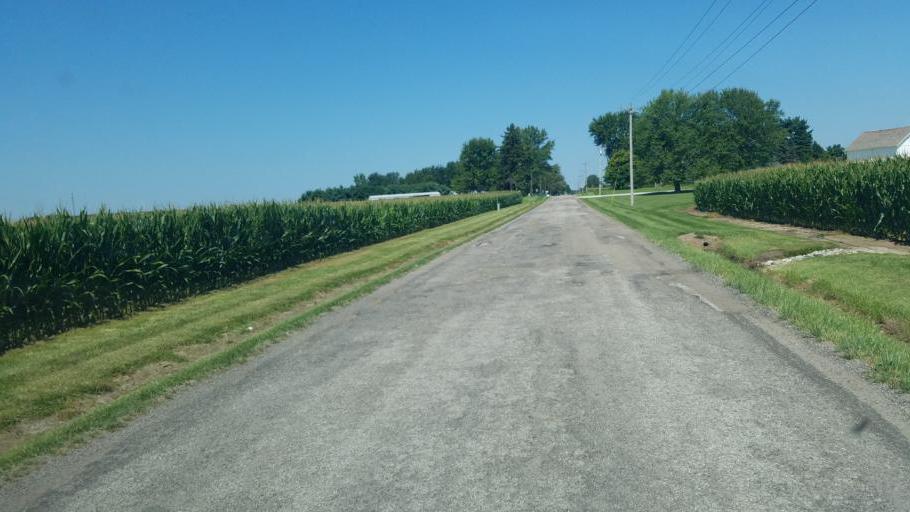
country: US
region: Ohio
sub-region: Delaware County
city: Ashley
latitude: 40.4268
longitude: -82.9600
